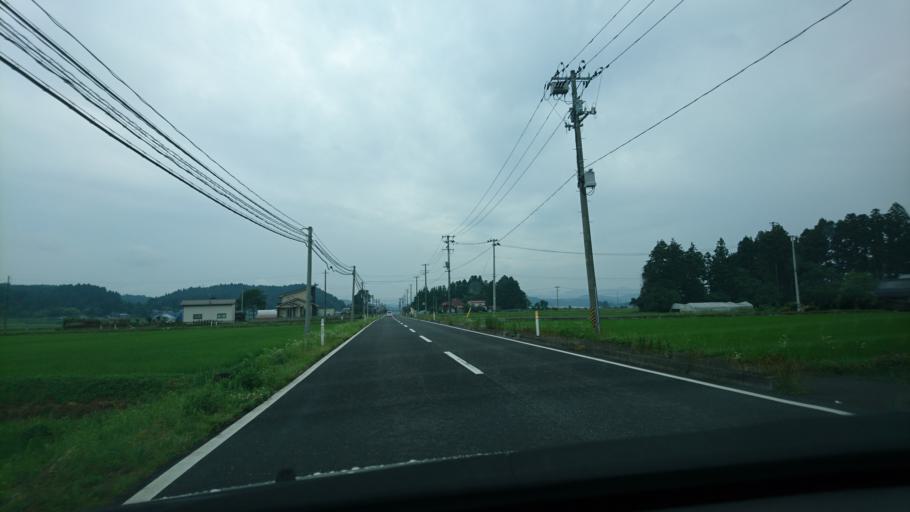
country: JP
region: Miyagi
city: Furukawa
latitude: 38.7399
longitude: 140.9395
